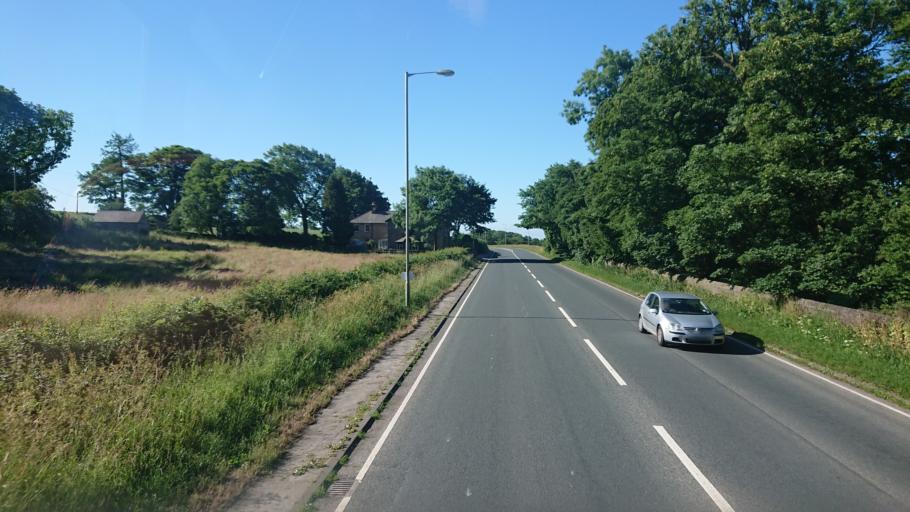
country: GB
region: England
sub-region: Lancashire
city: Galgate
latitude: 53.9780
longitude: -2.7849
